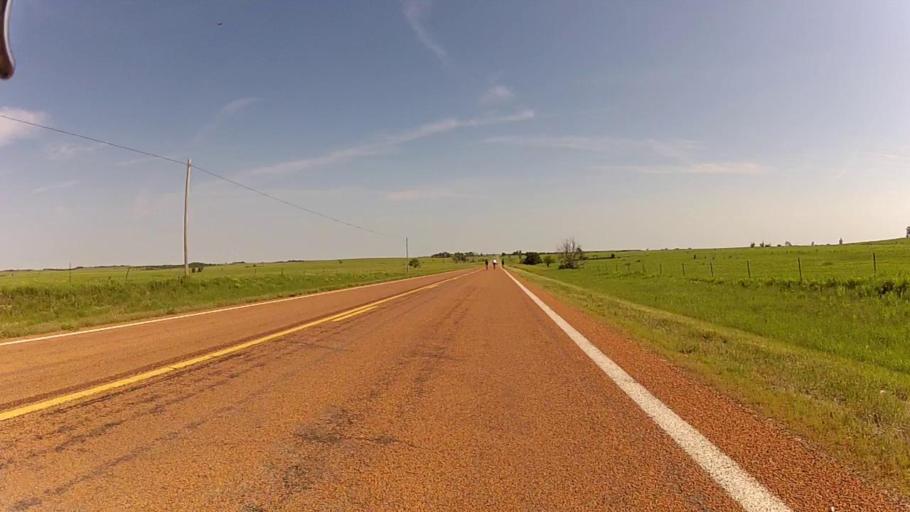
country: US
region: Kansas
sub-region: Cowley County
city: Winfield
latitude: 37.0727
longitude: -96.6436
